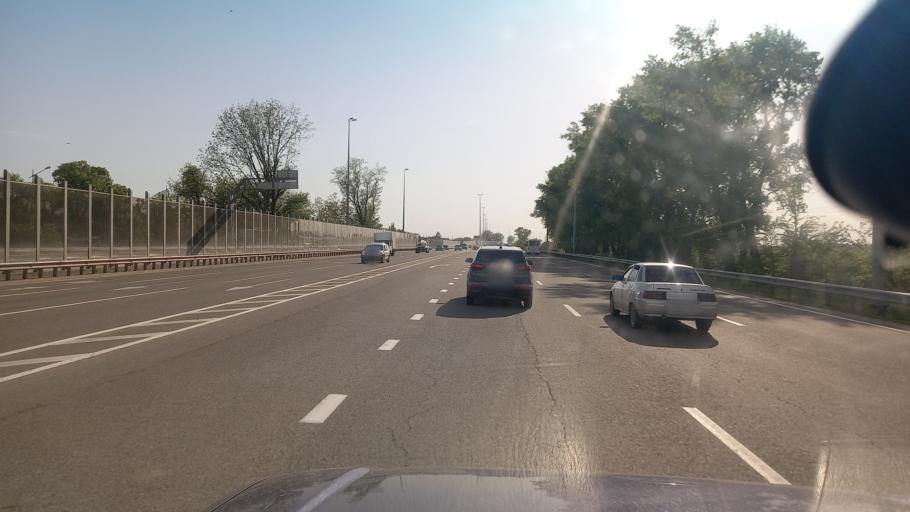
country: RU
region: Krasnodarskiy
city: Yelizavetinskaya
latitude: 45.0548
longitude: 38.8576
